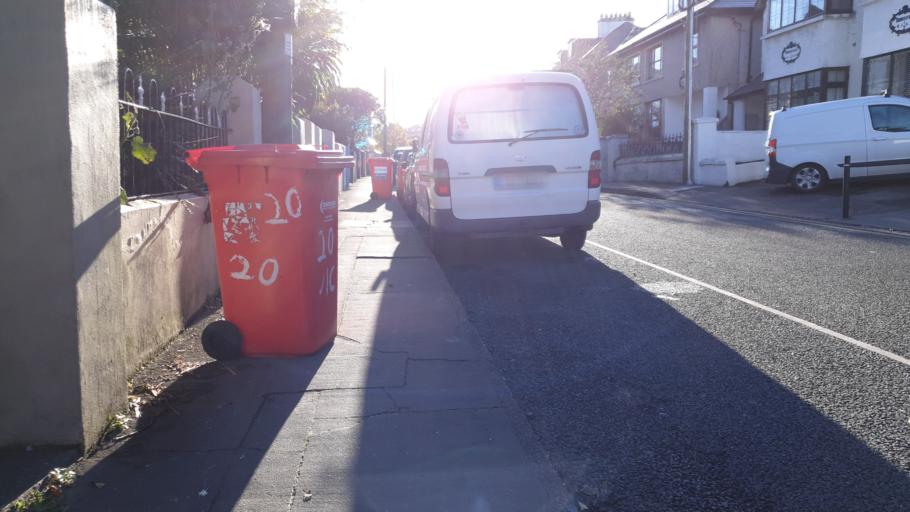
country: IE
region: Munster
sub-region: County Cork
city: Cork
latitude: 51.8926
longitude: -8.4548
